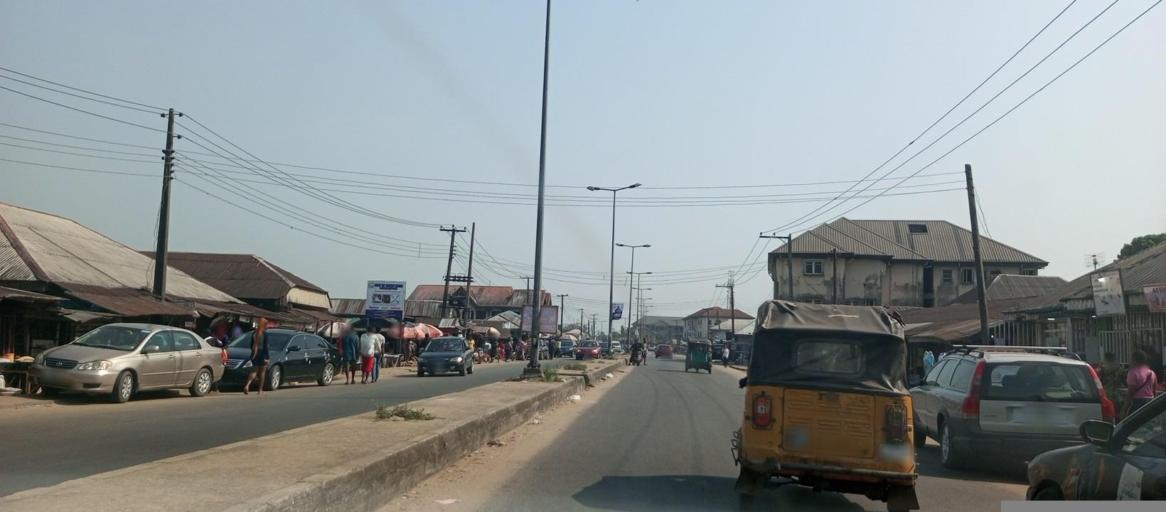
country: NG
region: Rivers
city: Emuoha
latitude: 4.8888
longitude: 6.9013
